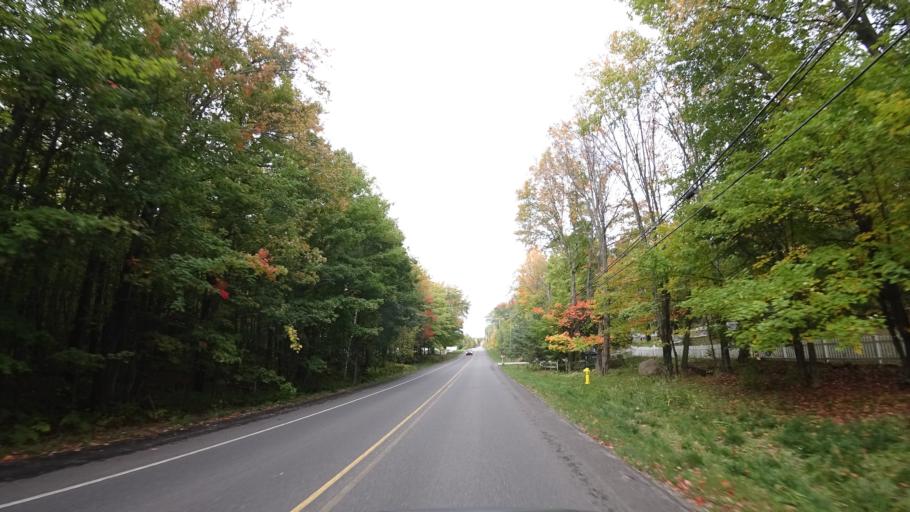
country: US
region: Michigan
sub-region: Marquette County
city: Trowbridge Park
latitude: 46.5377
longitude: -87.4374
